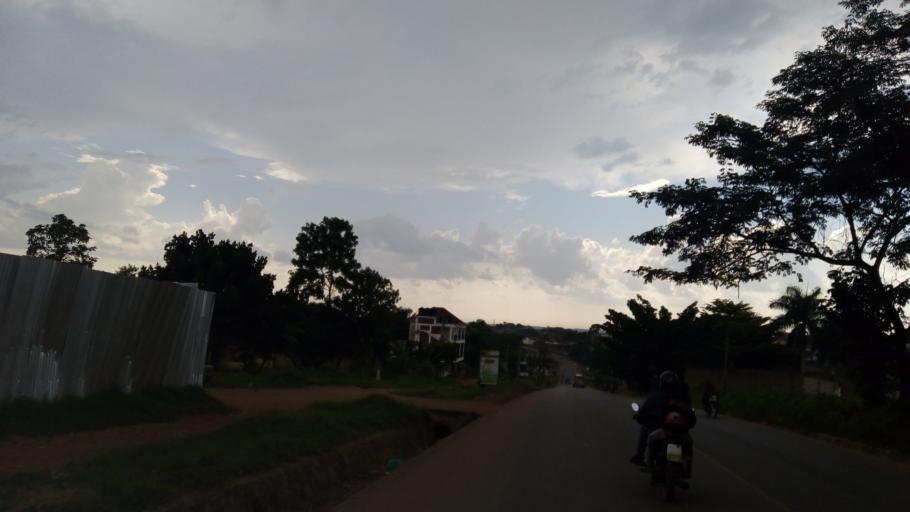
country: UG
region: Eastern Region
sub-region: Mbale District
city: Mbale
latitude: 1.0729
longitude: 34.1728
